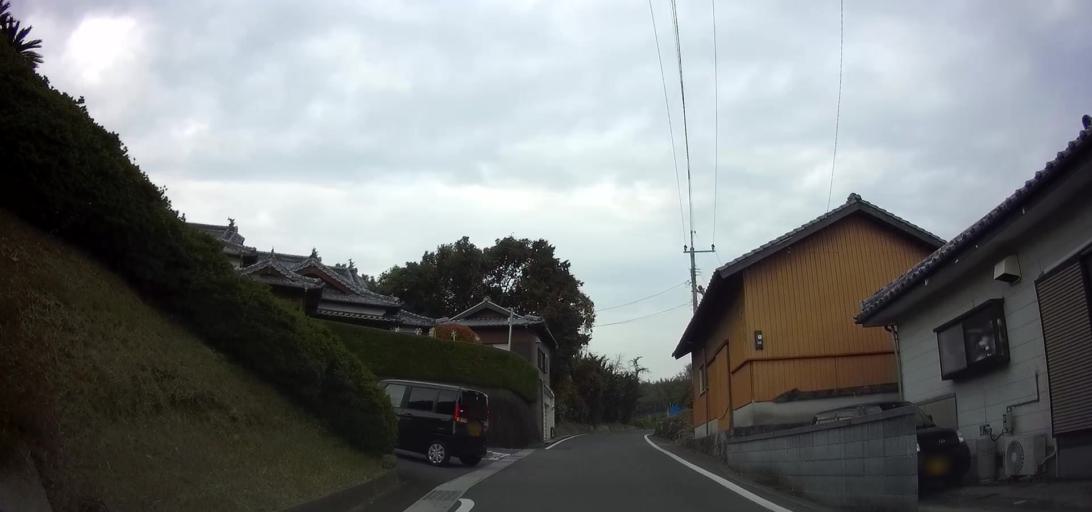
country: JP
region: Kumamoto
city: Hondo
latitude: 32.6367
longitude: 130.2430
